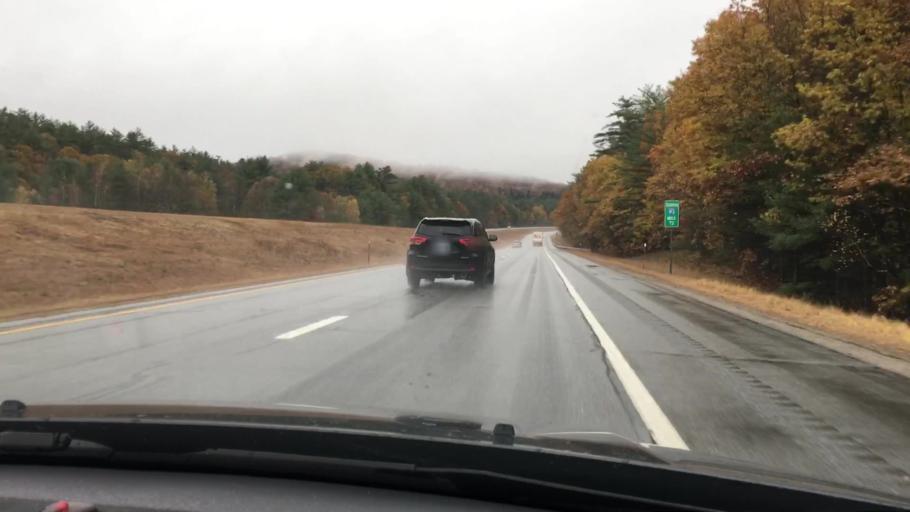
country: US
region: New Hampshire
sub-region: Grafton County
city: Ashland
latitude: 43.6517
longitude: -71.6484
